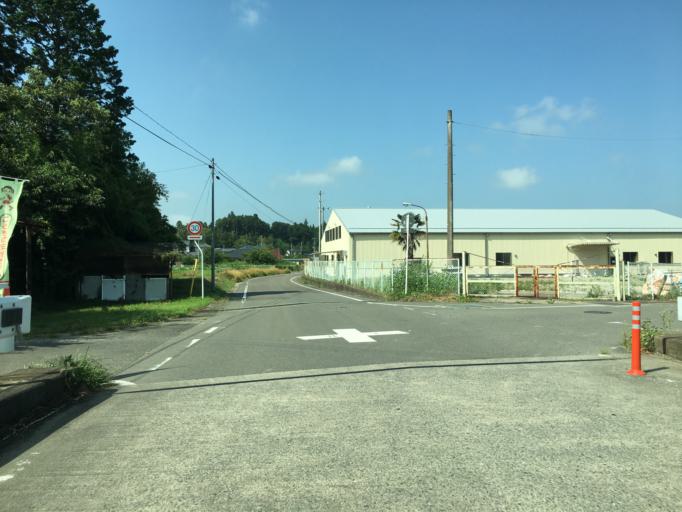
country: JP
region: Miyagi
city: Marumori
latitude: 37.8878
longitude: 140.8919
